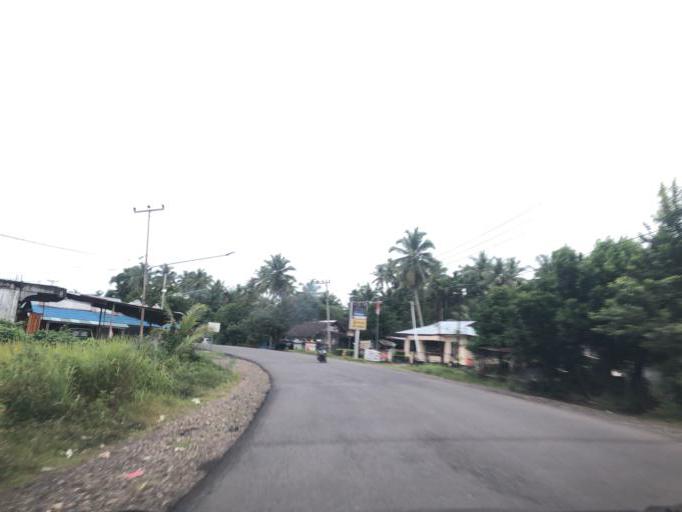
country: ID
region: West Sumatra
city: Pauhambar
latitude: -0.6442
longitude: 100.2130
